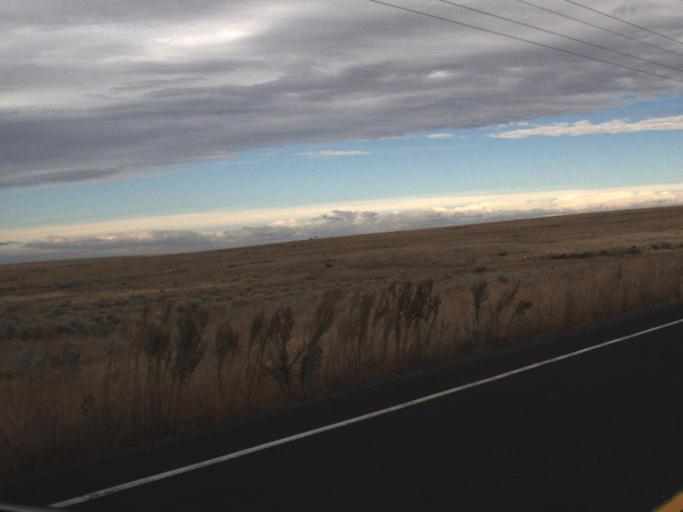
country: US
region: Washington
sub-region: Adams County
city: Ritzville
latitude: 47.4311
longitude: -118.7181
